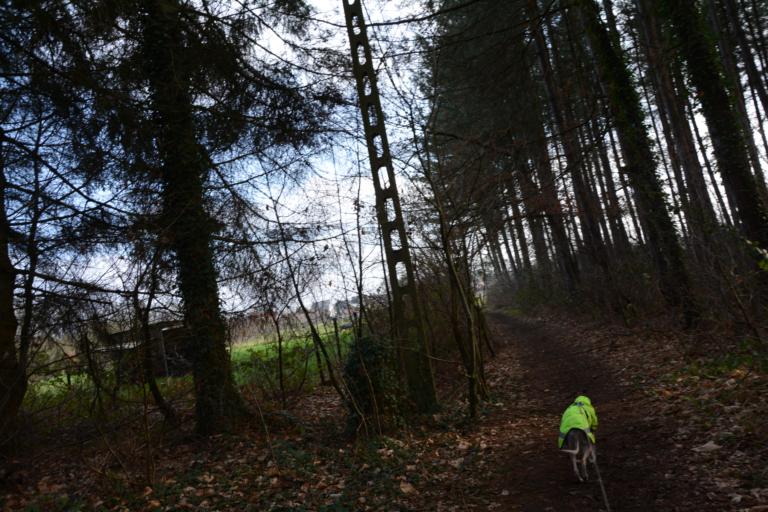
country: BE
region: Flanders
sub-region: Provincie Antwerpen
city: Herselt
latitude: 51.0320
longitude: 4.9121
